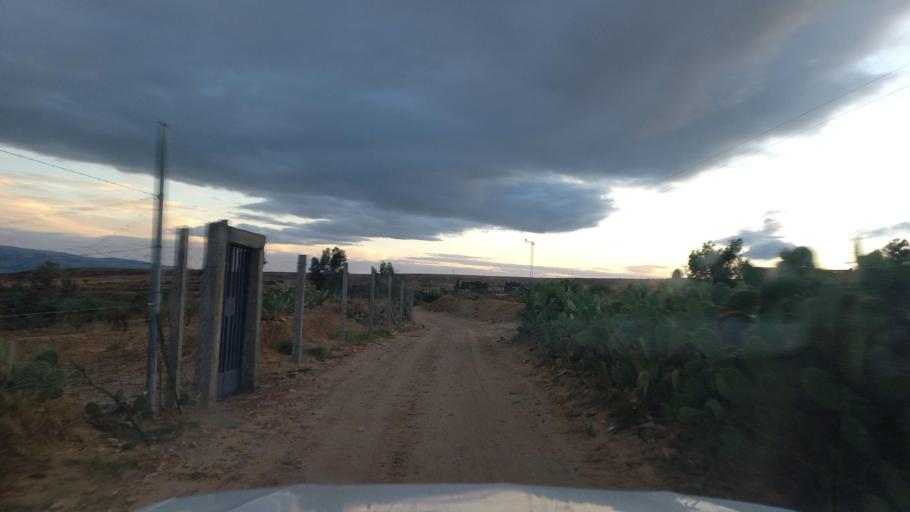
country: TN
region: Al Qasrayn
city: Kasserine
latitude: 35.2566
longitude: 8.9346
